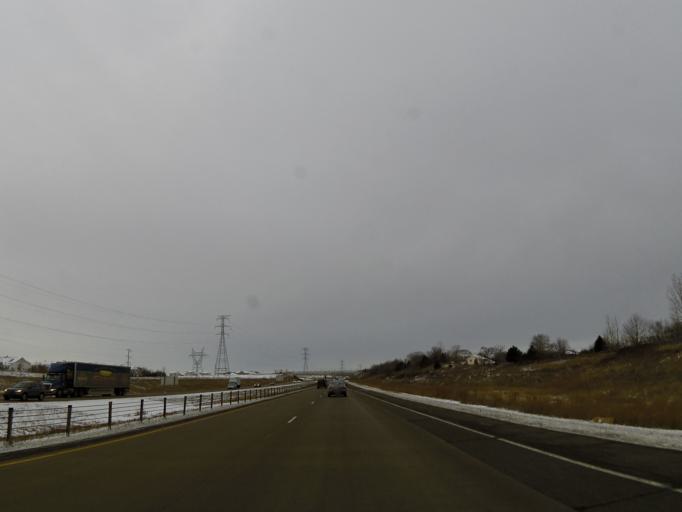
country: US
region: Minnesota
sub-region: Scott County
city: Shakopee
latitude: 44.7772
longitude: -93.5137
